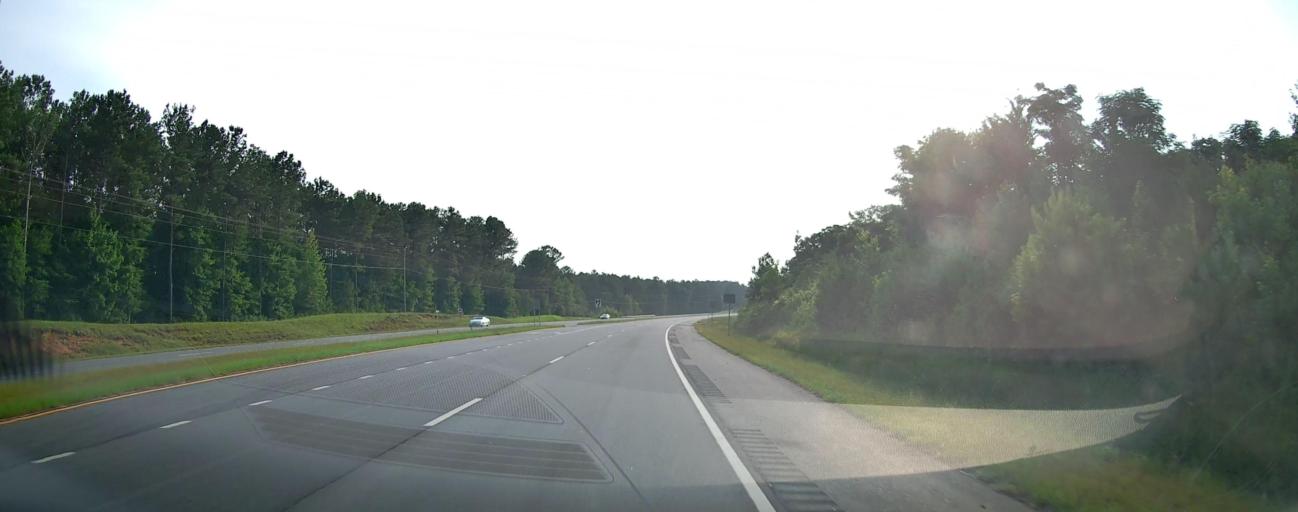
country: US
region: Georgia
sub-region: Talbot County
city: Talbotton
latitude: 32.5617
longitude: -84.6117
